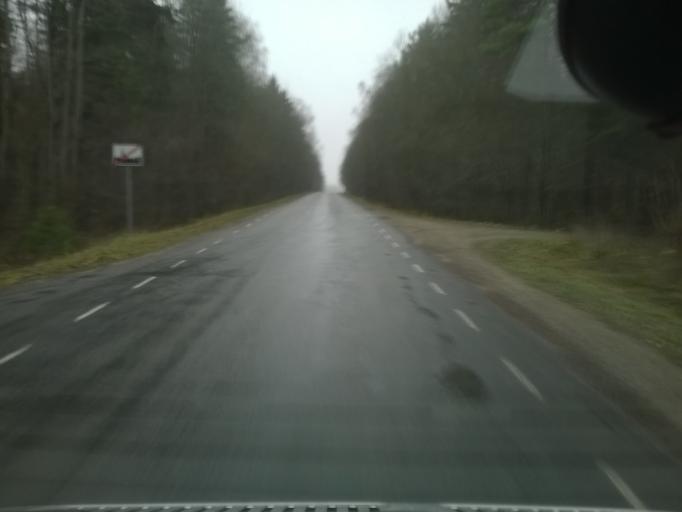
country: EE
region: Raplamaa
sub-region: Kohila vald
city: Kohila
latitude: 59.1755
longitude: 24.6562
